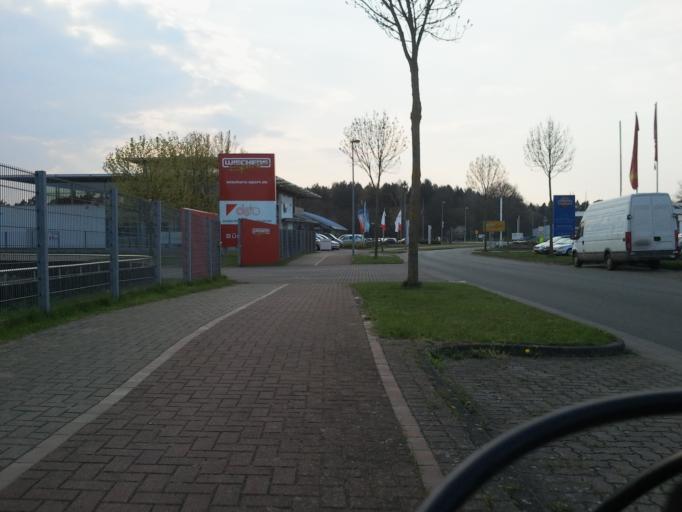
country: DE
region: Lower Saxony
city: Nienburg
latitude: 52.6194
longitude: 9.2035
